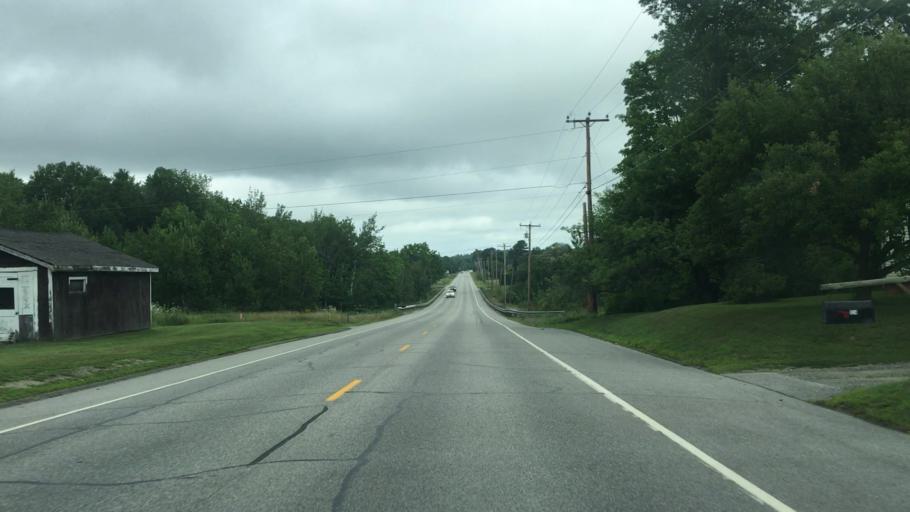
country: US
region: Maine
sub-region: Kennebec County
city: Pittston
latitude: 44.1486
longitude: -69.7436
